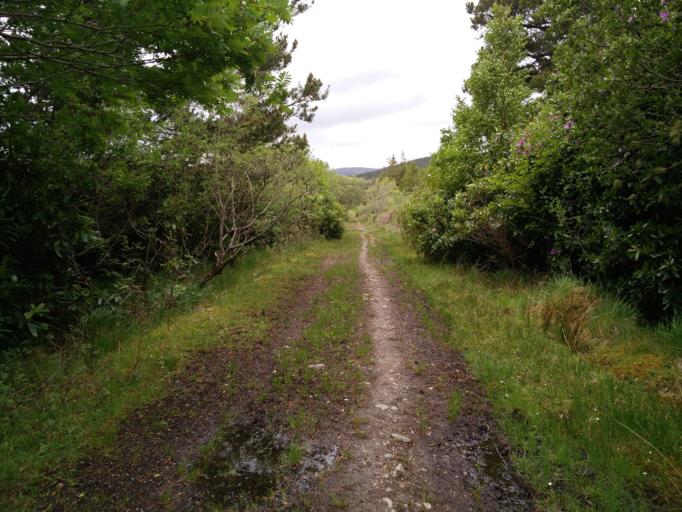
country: IE
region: Connaught
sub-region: Maigh Eo
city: Westport
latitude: 53.9860
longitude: -9.5708
